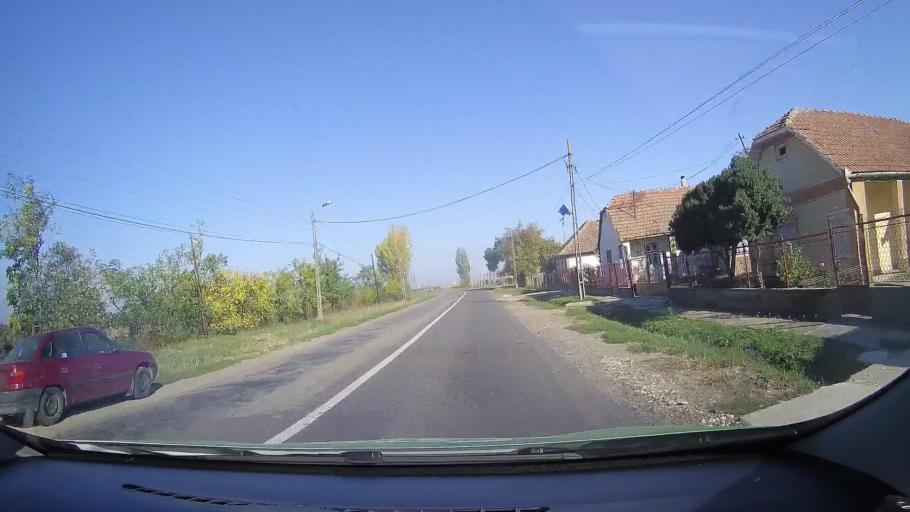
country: RO
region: Satu Mare
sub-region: Oras Tasnad
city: Tasnad
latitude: 47.5143
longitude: 22.5724
